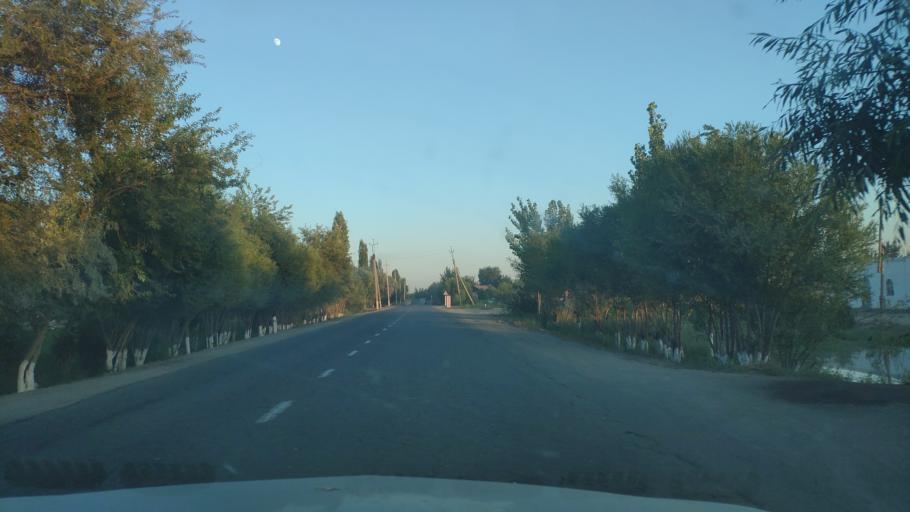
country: UZ
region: Karakalpakstan
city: To'rtko'l Shahri
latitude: 41.5650
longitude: 60.9531
